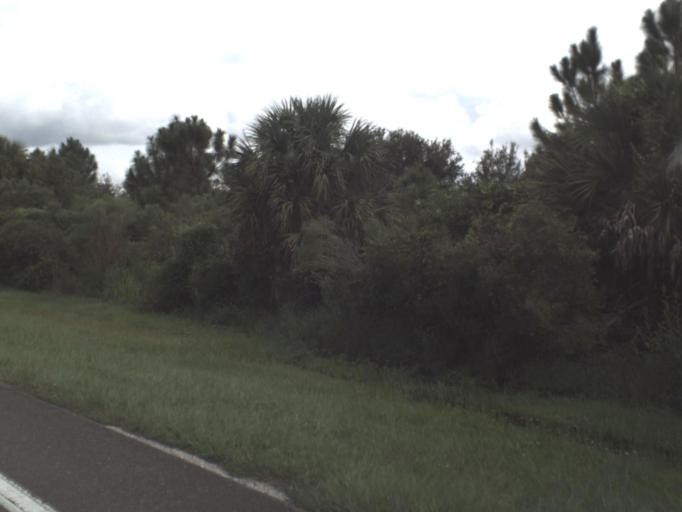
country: US
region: Florida
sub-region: DeSoto County
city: Nocatee
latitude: 27.2040
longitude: -82.0581
